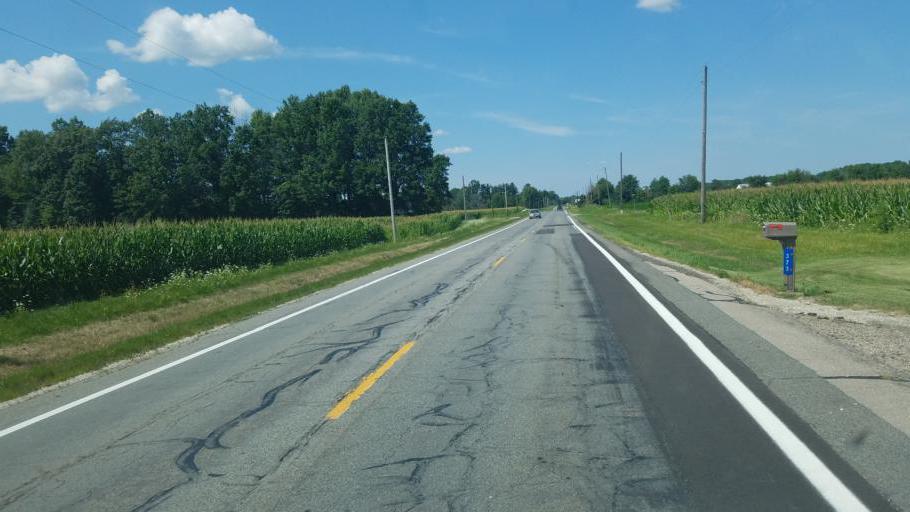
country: US
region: Ohio
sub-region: Crawford County
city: Galion
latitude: 40.7179
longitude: -82.7650
